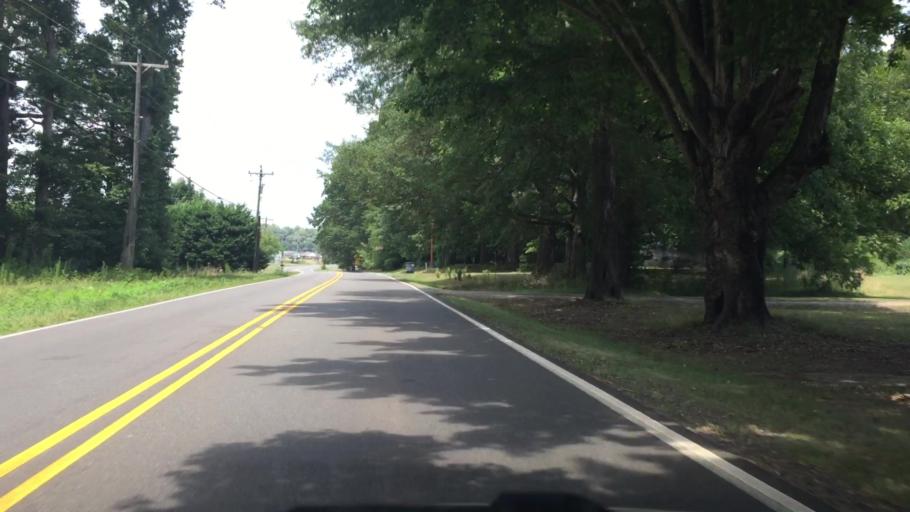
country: US
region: North Carolina
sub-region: Iredell County
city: Troutman
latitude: 35.7195
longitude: -80.8741
